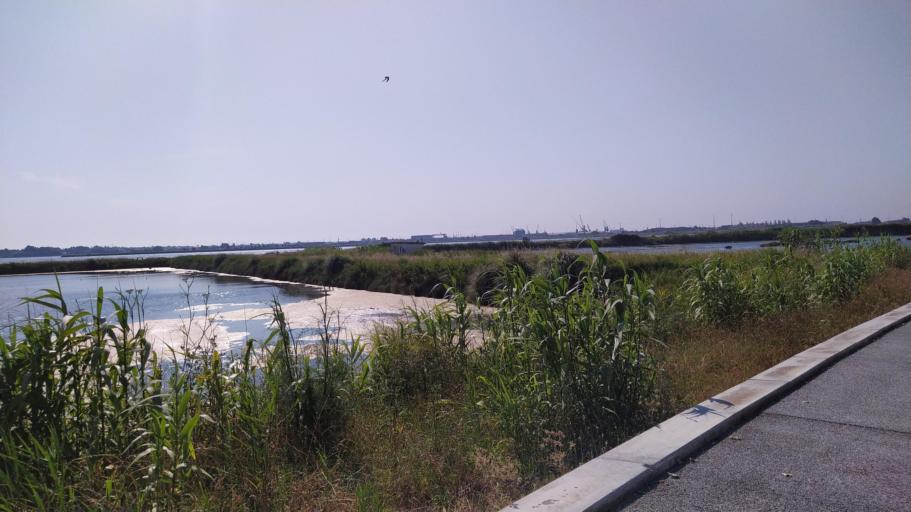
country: PT
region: Aveiro
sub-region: Aveiro
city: Aveiro
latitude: 40.6307
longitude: -8.6615
